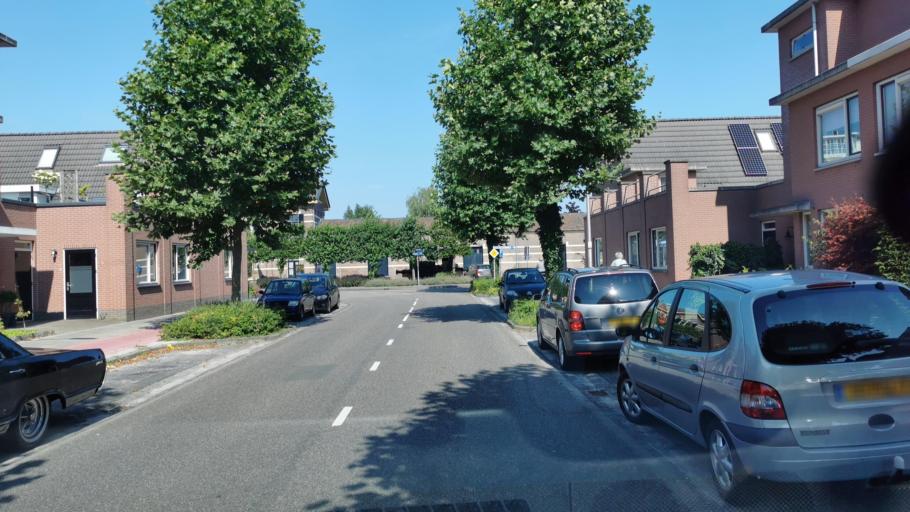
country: NL
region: Overijssel
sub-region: Gemeente Haaksbergen
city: Haaksbergen
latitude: 52.1580
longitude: 6.7391
